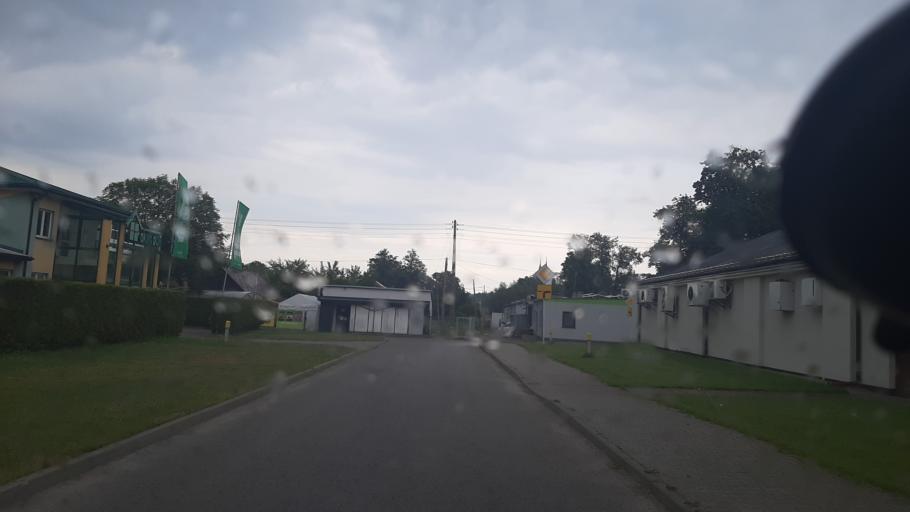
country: PL
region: Lublin Voivodeship
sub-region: Powiat lubelski
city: Garbow
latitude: 51.3551
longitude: 22.3335
